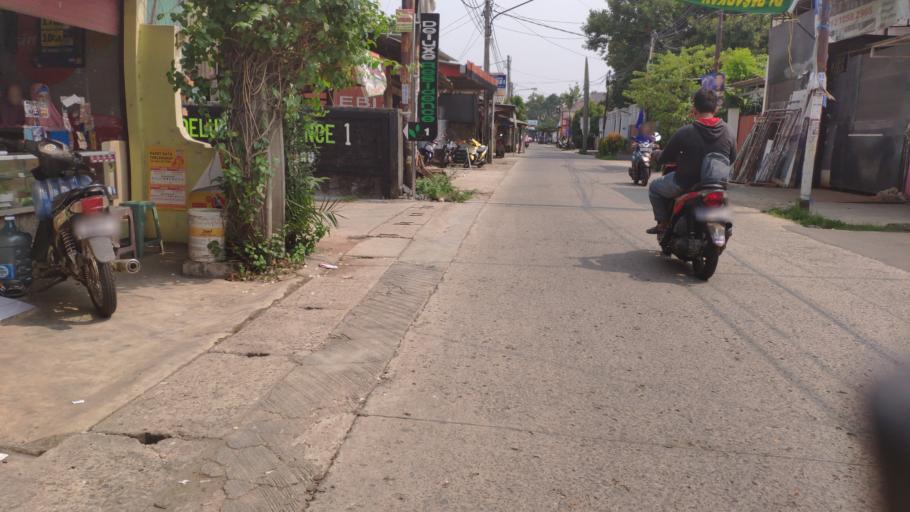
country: ID
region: West Java
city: Depok
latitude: -6.3780
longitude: 106.8016
